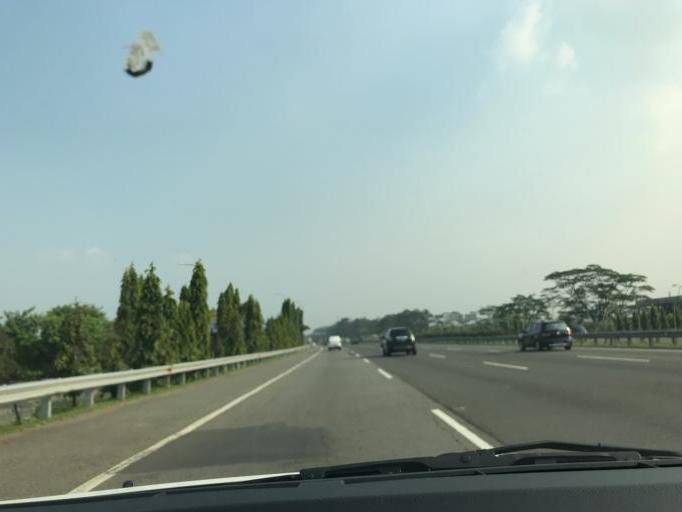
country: ID
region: West Java
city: Citeureup
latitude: -6.4857
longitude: 106.8727
